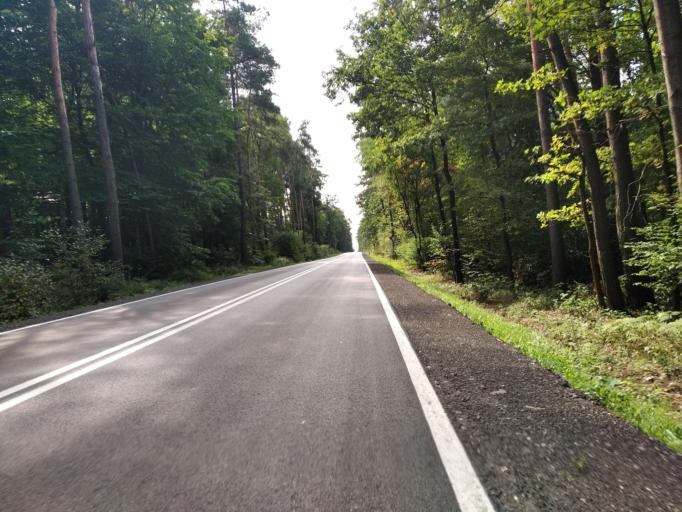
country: PL
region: Subcarpathian Voivodeship
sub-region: Powiat ropczycko-sedziszowski
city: Ostrow
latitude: 50.1299
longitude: 21.5881
